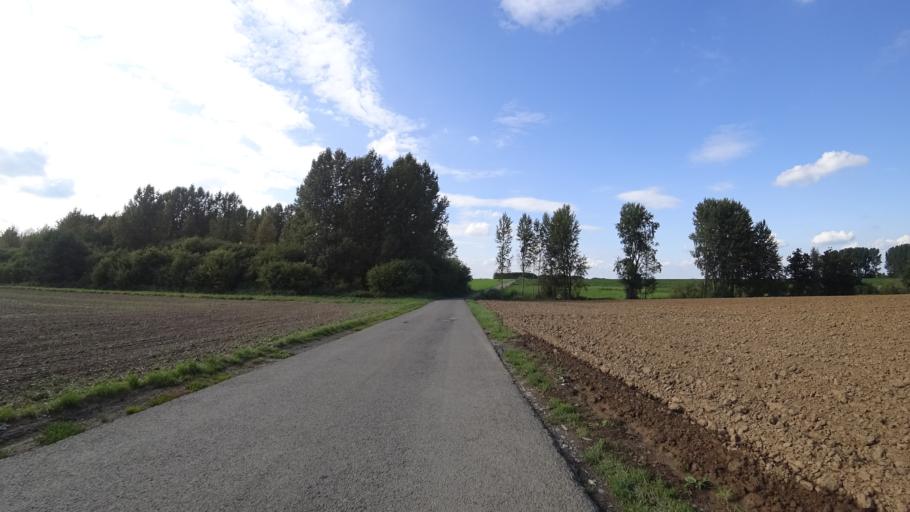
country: BE
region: Wallonia
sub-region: Province de Namur
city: Sombreffe
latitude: 50.5518
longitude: 4.6374
